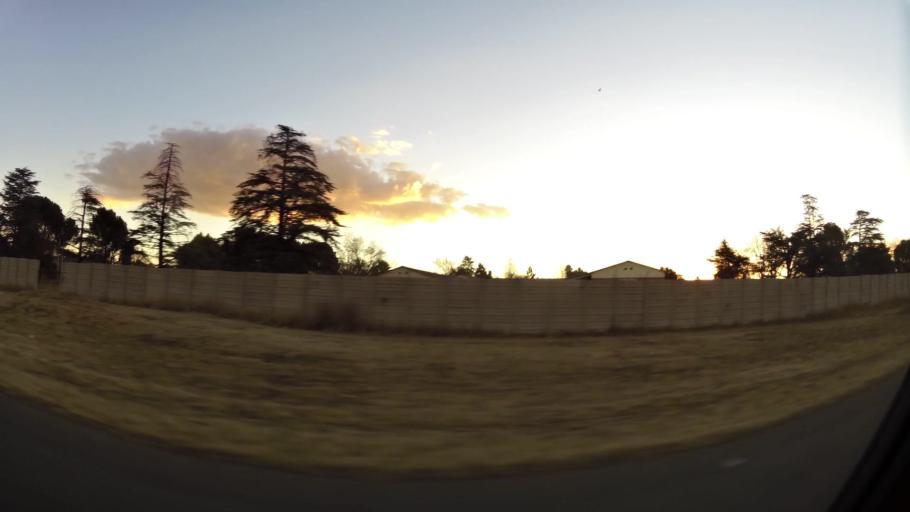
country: ZA
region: North-West
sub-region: Dr Kenneth Kaunda District Municipality
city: Potchefstroom
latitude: -26.6806
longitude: 27.0753
